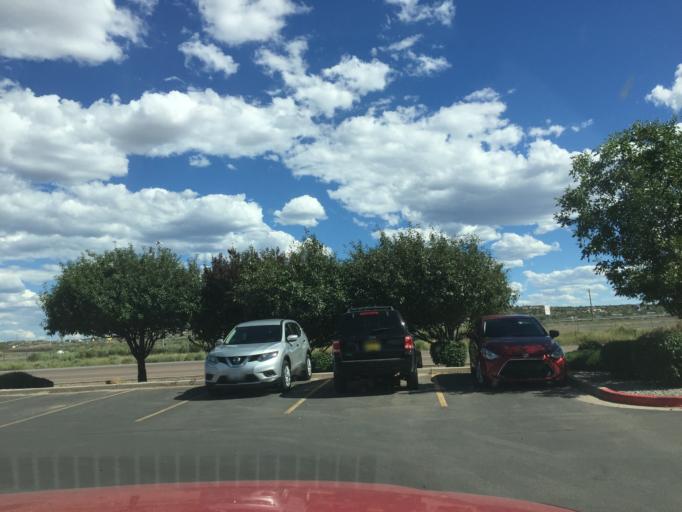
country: US
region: New Mexico
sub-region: McKinley County
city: Gallup
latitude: 35.5283
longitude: -108.7641
